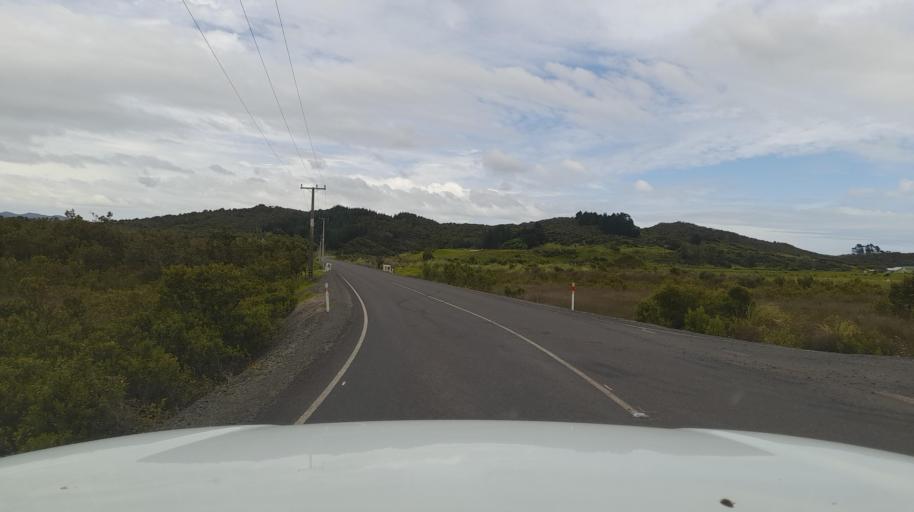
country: NZ
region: Northland
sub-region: Far North District
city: Kaitaia
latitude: -35.4008
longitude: 173.3819
